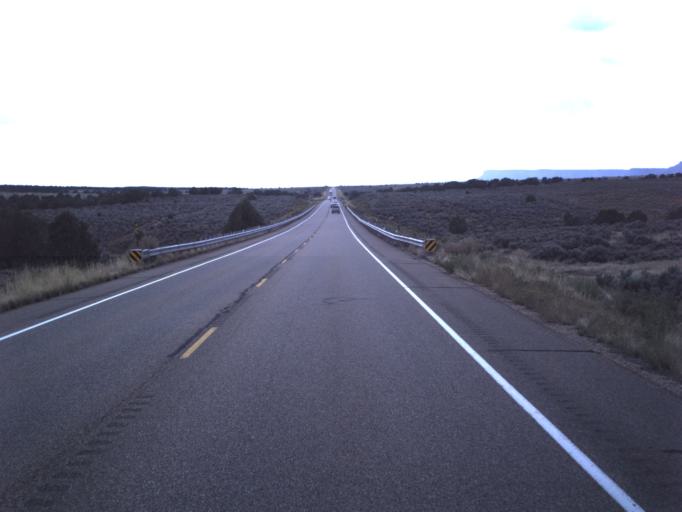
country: US
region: Utah
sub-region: Kane County
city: Kanab
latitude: 37.1817
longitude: -112.0033
